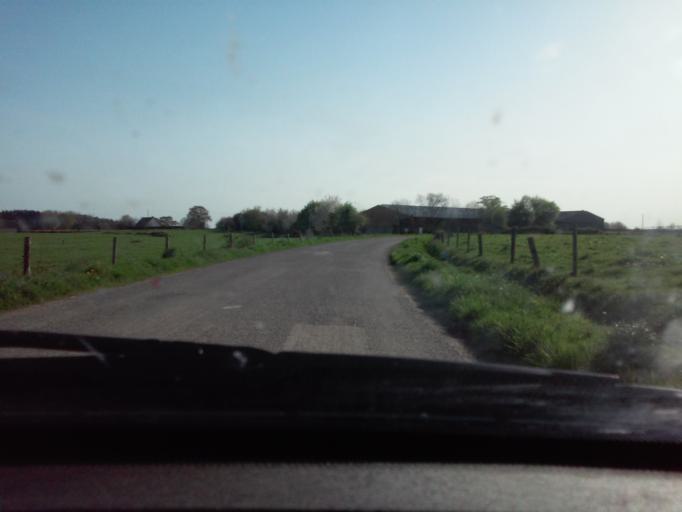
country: FR
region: Brittany
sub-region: Departement d'Ille-et-Vilaine
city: Romagne
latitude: 48.3041
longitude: -1.2648
